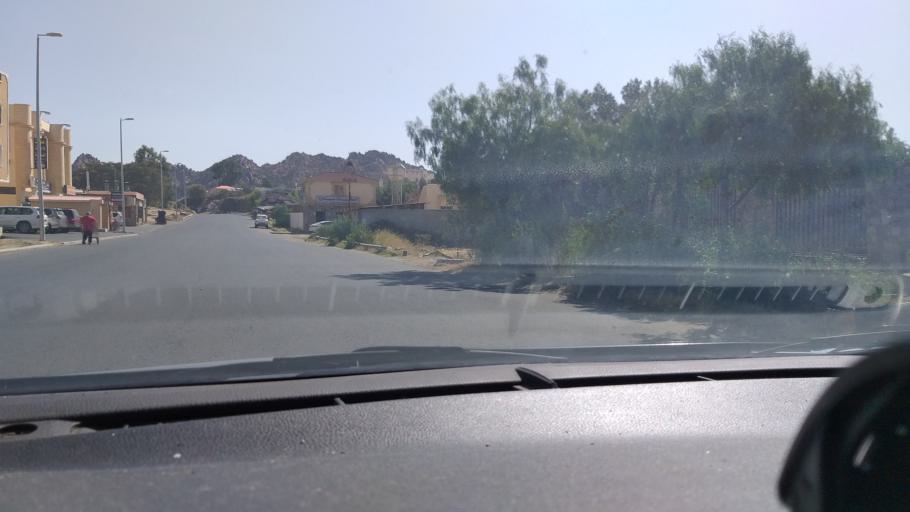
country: SA
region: Makkah
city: Ash Shafa
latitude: 21.0669
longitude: 40.3220
